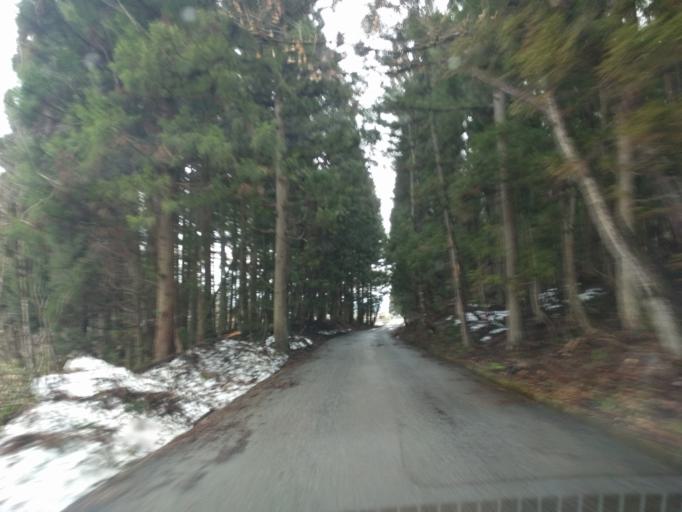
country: JP
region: Fukushima
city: Kitakata
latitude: 37.6760
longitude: 139.9199
